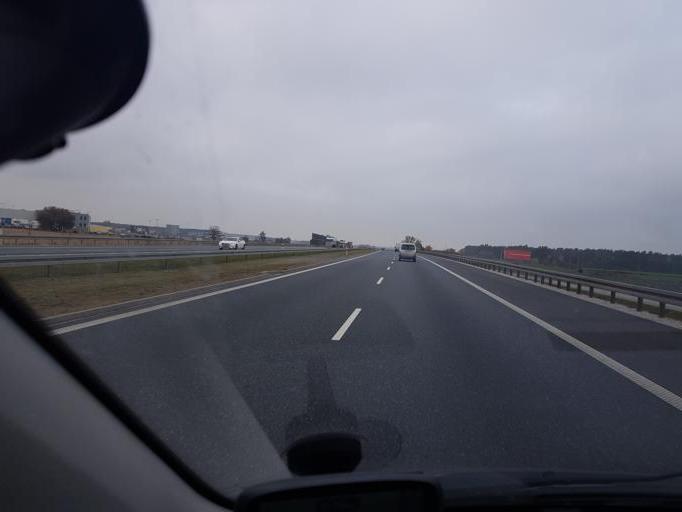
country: PL
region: Kujawsko-Pomorskie
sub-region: Powiat wloclawski
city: Brzesc Kujawski
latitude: 52.6264
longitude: 18.9618
